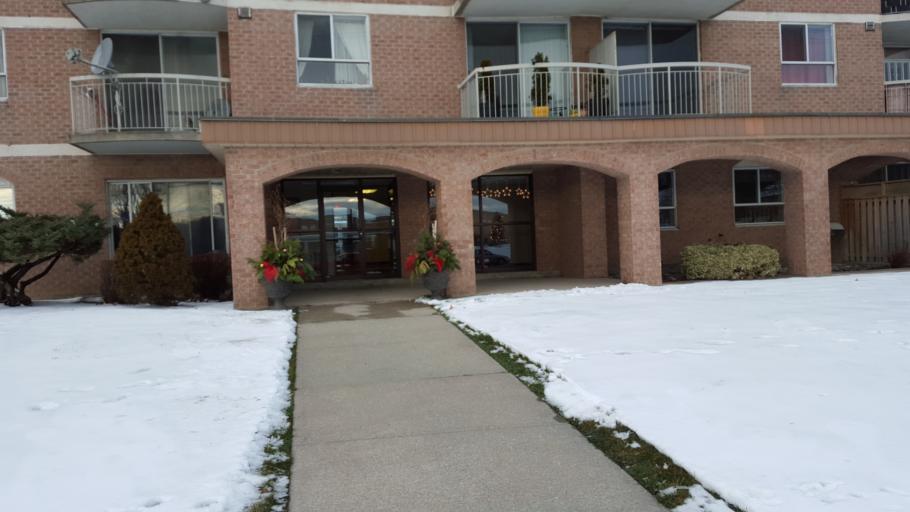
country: CA
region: Ontario
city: Kingston
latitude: 44.2403
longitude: -76.5200
